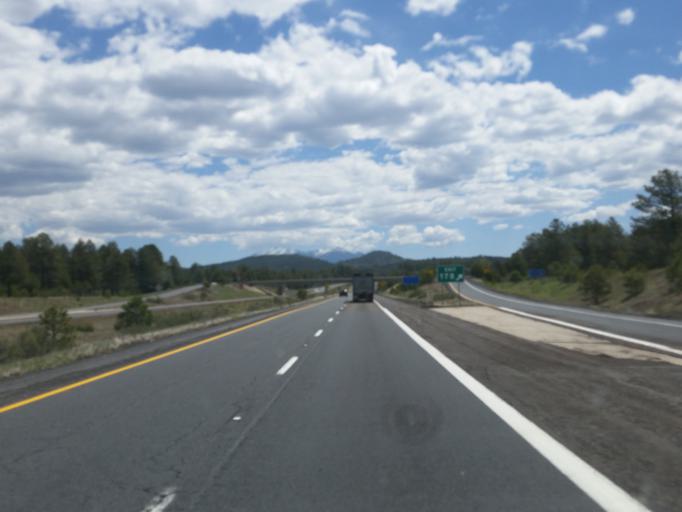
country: US
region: Arizona
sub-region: Coconino County
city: Parks
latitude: 35.2544
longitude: -111.9428
